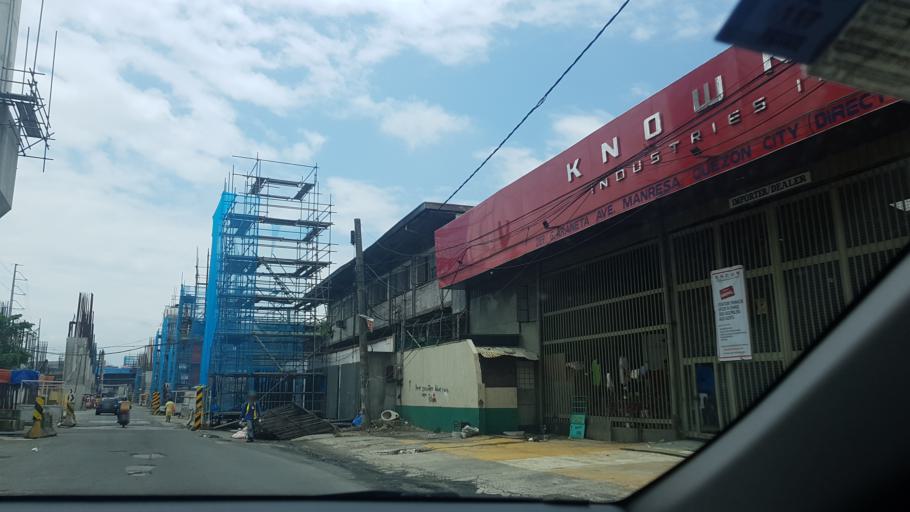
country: PH
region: Calabarzon
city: Del Monte
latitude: 14.6429
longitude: 121.0058
